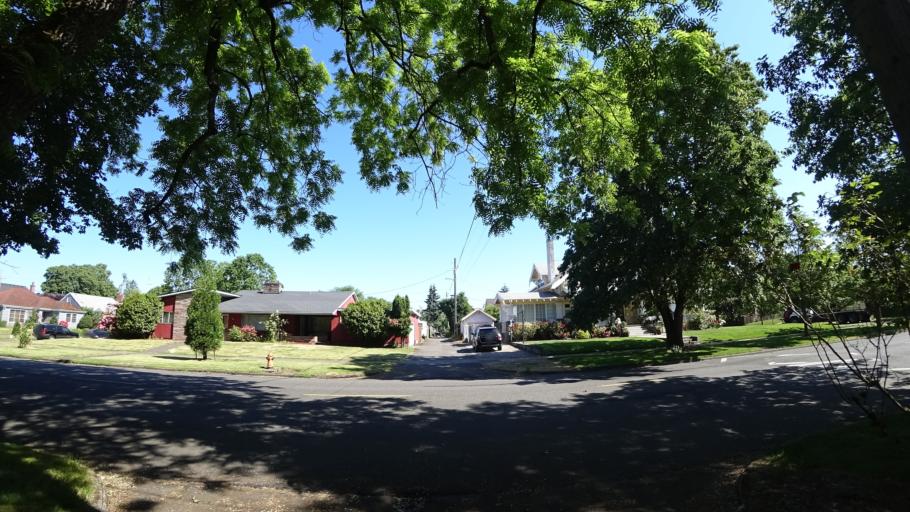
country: US
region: Oregon
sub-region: Multnomah County
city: Portland
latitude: 45.5663
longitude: -122.6653
